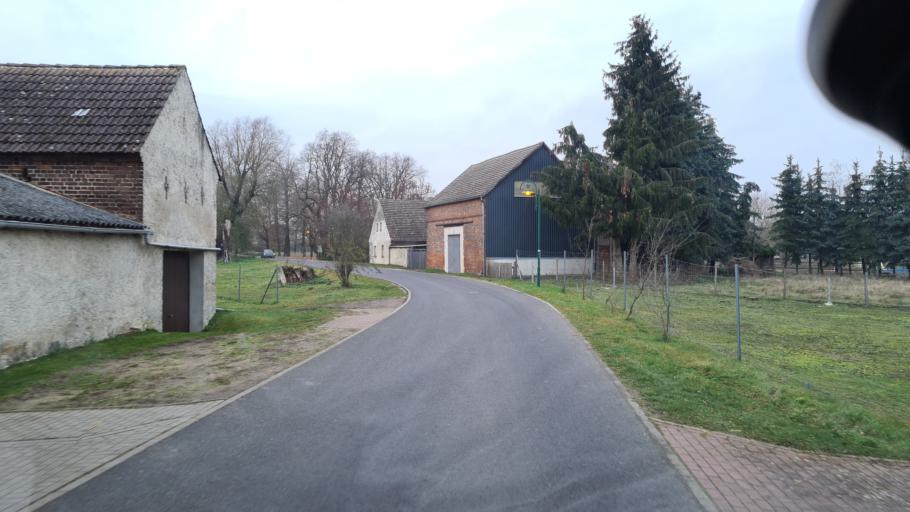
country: DE
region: Brandenburg
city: Schenkendobern
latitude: 51.9594
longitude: 14.6311
